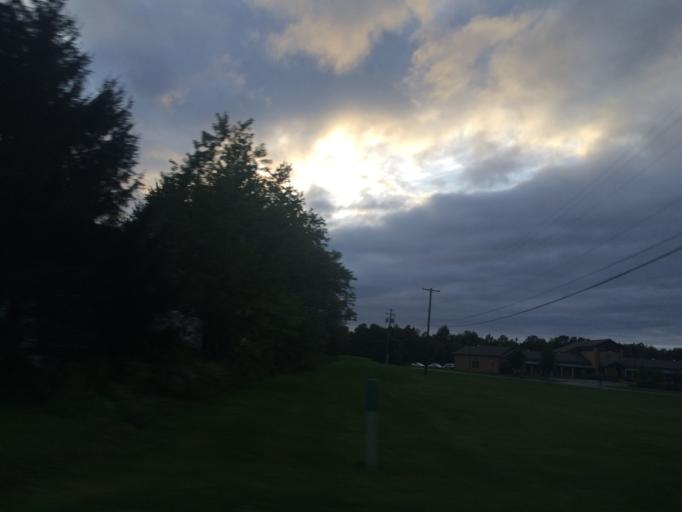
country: US
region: New York
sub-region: Erie County
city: Elma Center
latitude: 42.8140
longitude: -78.6368
